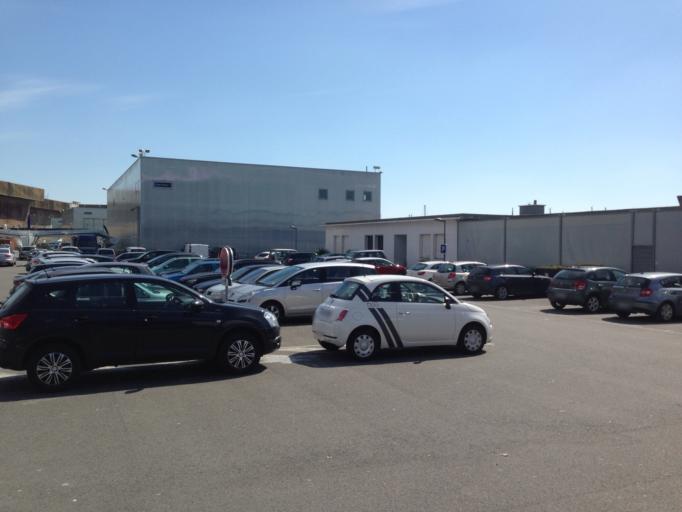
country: FR
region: Brittany
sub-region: Departement du Morbihan
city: Lorient
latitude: 47.7305
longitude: -3.3736
